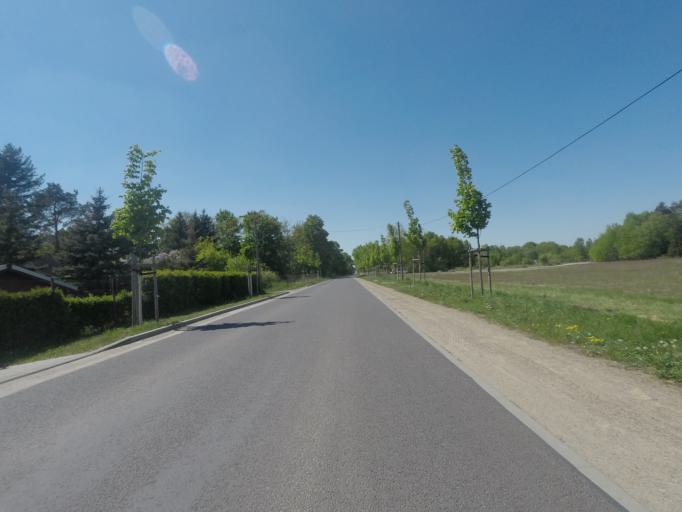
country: DE
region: Brandenburg
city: Melchow
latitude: 52.8507
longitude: 13.7066
